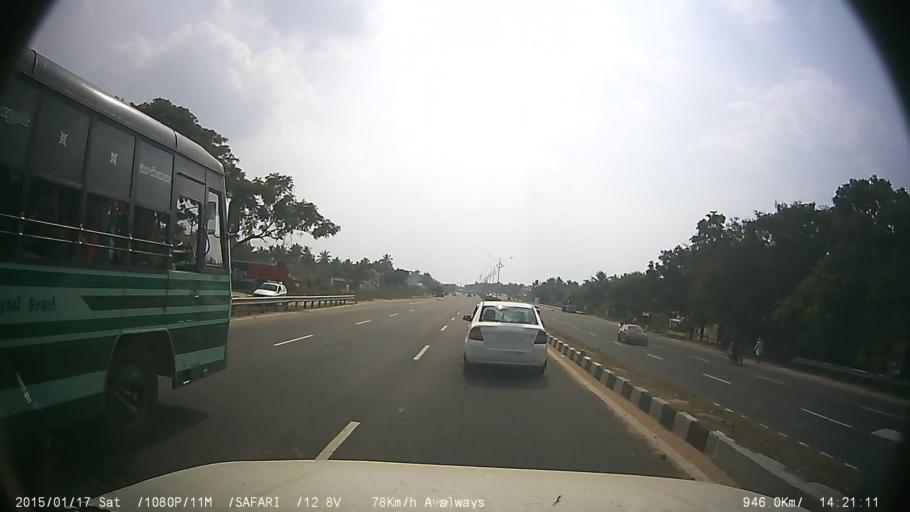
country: IN
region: Tamil Nadu
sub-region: Vellore
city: Vaniyambadi
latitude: 12.7007
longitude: 78.6437
